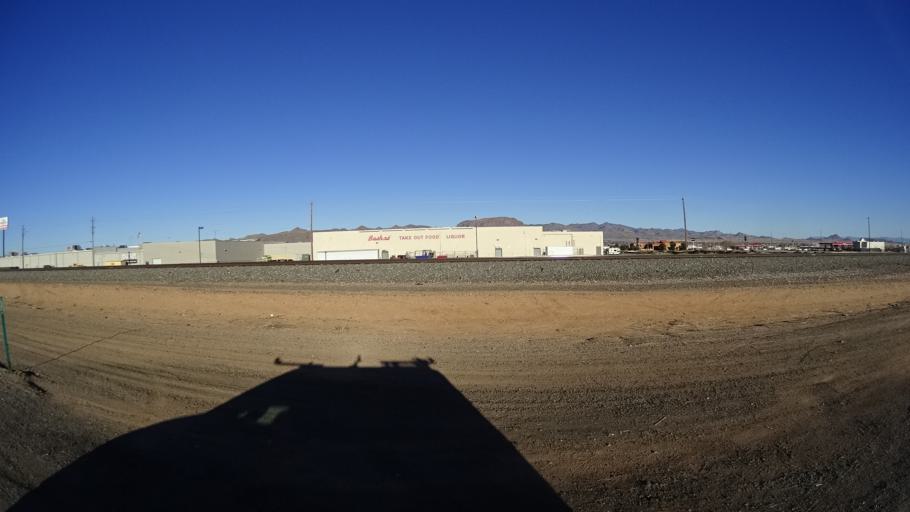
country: US
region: Arizona
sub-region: Mohave County
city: New Kingman-Butler
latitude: 35.2207
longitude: -114.0032
